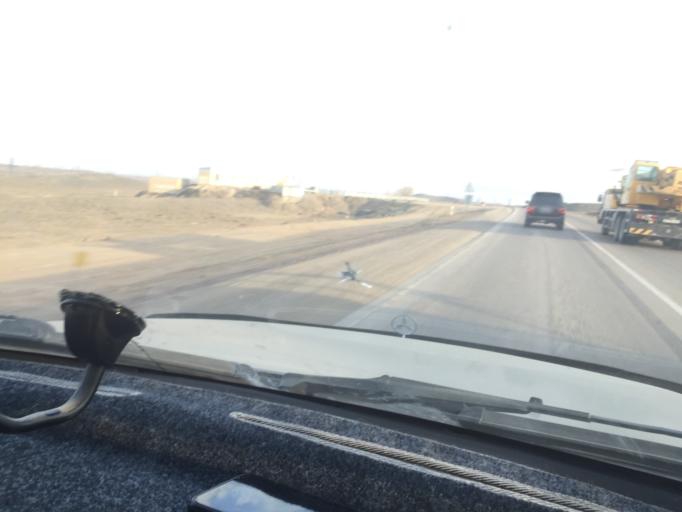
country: KZ
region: Almaty Oblysy
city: Ulken
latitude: 45.2039
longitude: 73.8882
